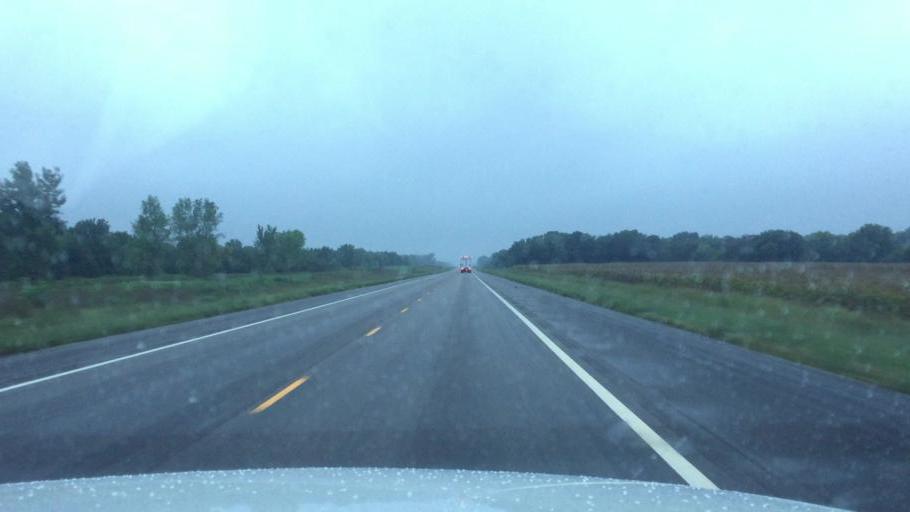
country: US
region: Kansas
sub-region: Montgomery County
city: Cherryvale
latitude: 37.4385
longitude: -95.4868
